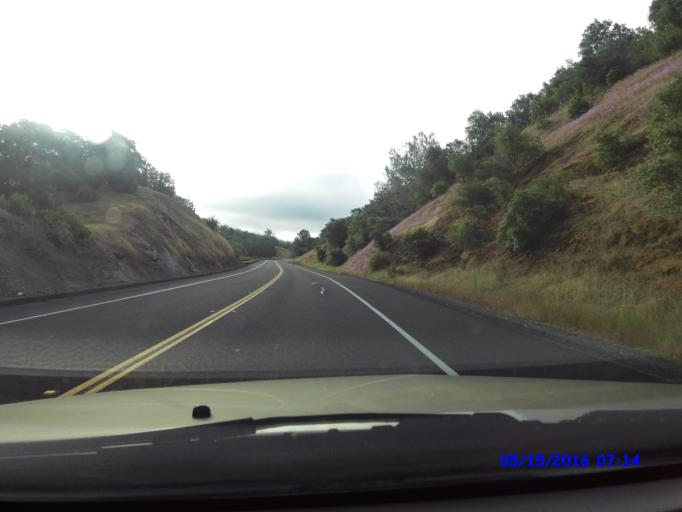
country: US
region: California
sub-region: Tuolumne County
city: Jamestown
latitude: 37.8315
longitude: -120.3531
